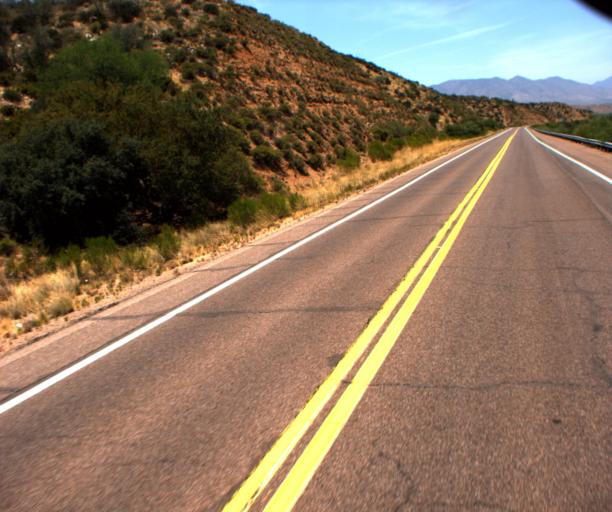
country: US
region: Arizona
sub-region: Gila County
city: Tonto Basin
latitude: 33.7443
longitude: -111.2289
